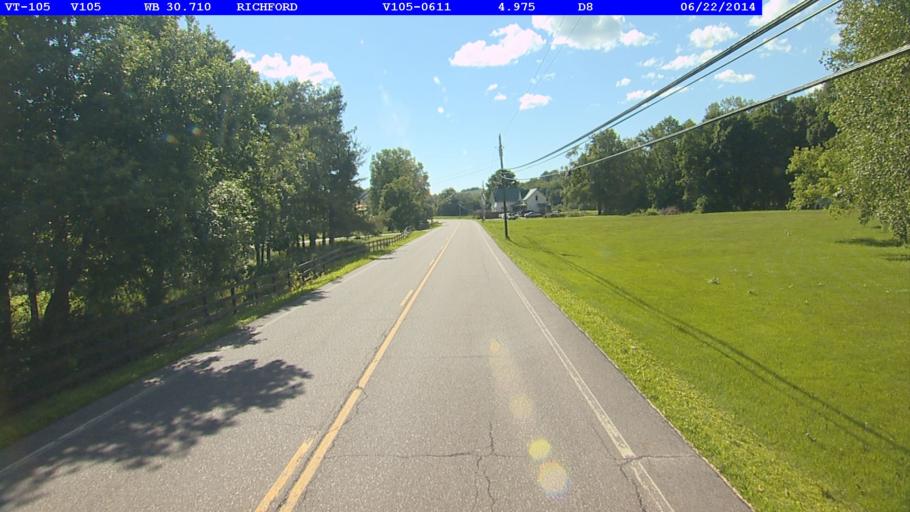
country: US
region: Vermont
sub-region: Franklin County
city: Richford
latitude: 44.9959
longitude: -72.6217
